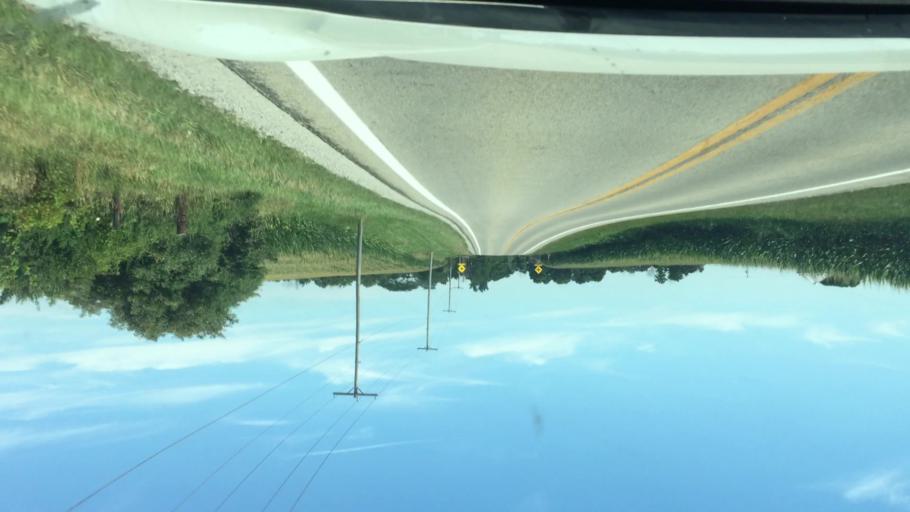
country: US
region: Ohio
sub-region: Clark County
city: Lisbon
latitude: 39.9418
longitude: -83.6115
